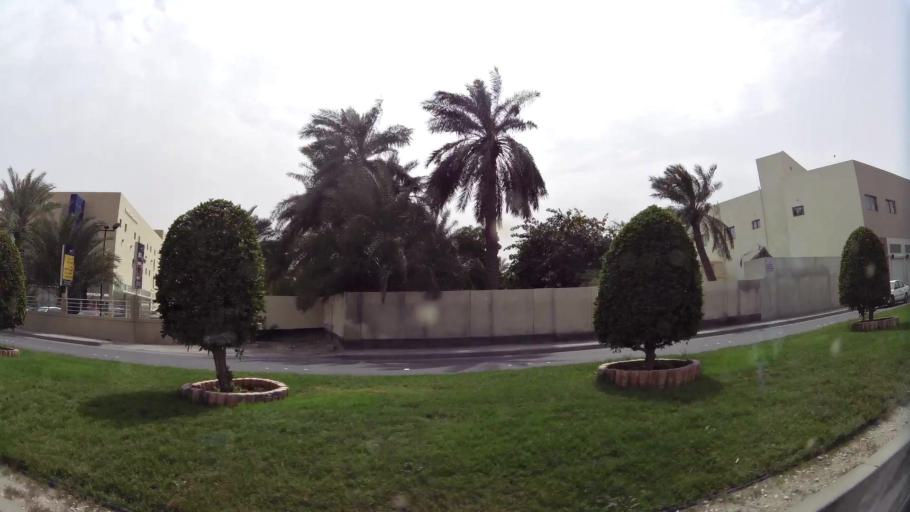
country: BH
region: Northern
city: Ar Rifa'
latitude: 26.1314
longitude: 50.5456
